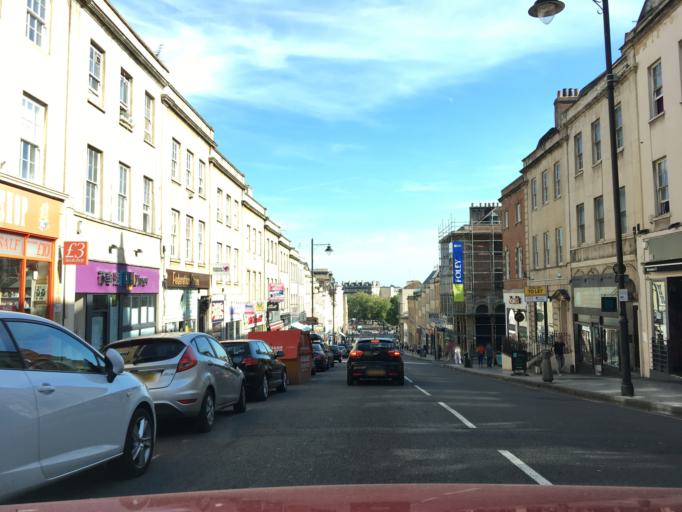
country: GB
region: England
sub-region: Bristol
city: Bristol
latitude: 51.4548
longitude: -2.6031
